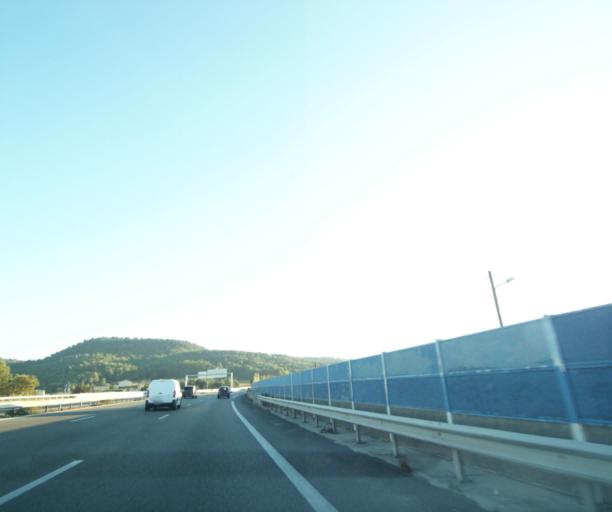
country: FR
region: Provence-Alpes-Cote d'Azur
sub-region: Departement des Bouches-du-Rhone
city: Roquefort-la-Bedoule
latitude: 43.2485
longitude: 5.5962
